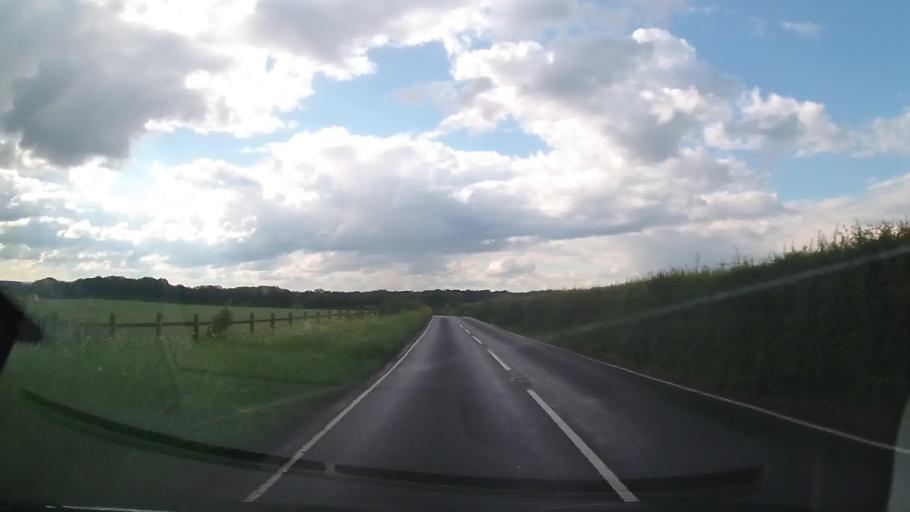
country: GB
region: England
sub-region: Shropshire
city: Withington
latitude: 52.6755
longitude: -2.6446
